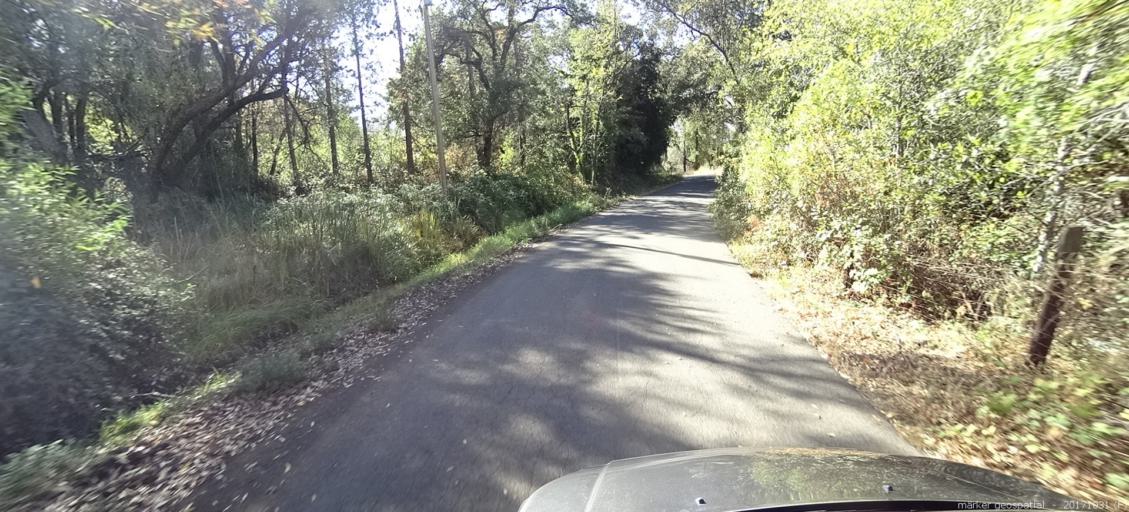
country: US
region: California
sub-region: Shasta County
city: Shingletown
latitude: 40.5252
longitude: -121.9563
